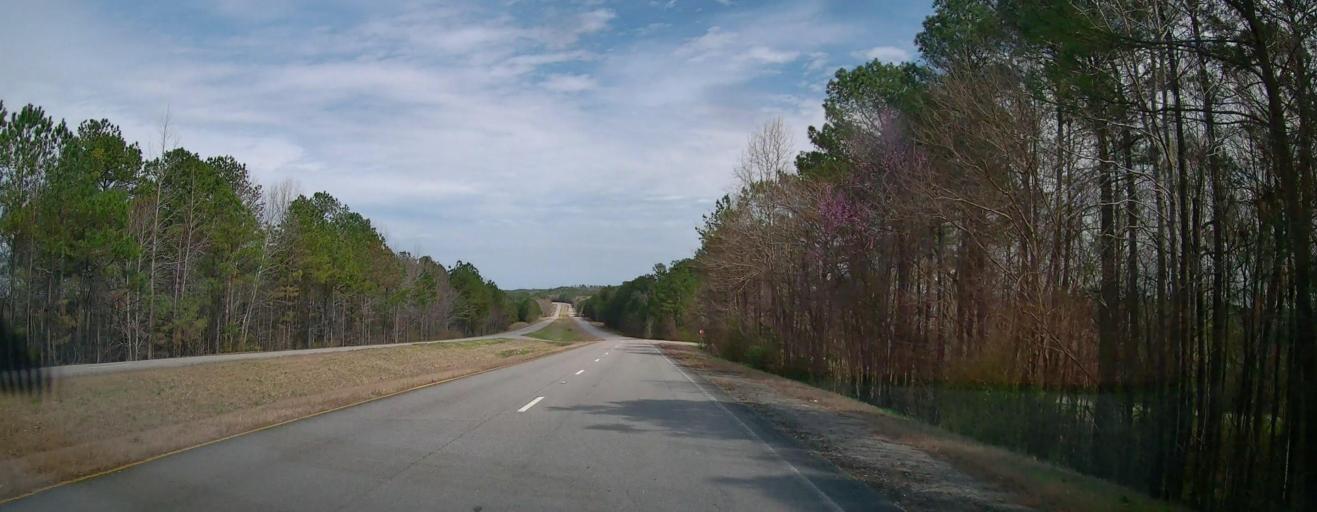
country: US
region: Alabama
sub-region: Marion County
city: Winfield
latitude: 33.9308
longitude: -87.6926
